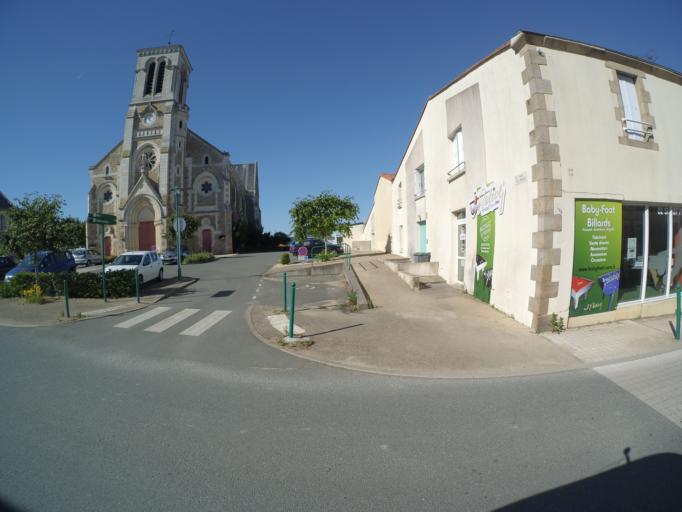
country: FR
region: Pays de la Loire
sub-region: Departement de la Vendee
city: Beaurepaire
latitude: 46.9076
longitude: -1.1332
